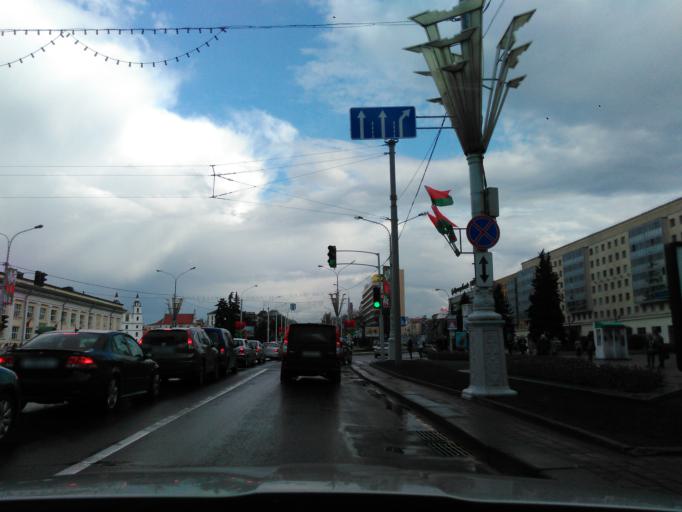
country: BY
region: Minsk
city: Minsk
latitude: 53.9075
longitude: 27.5511
